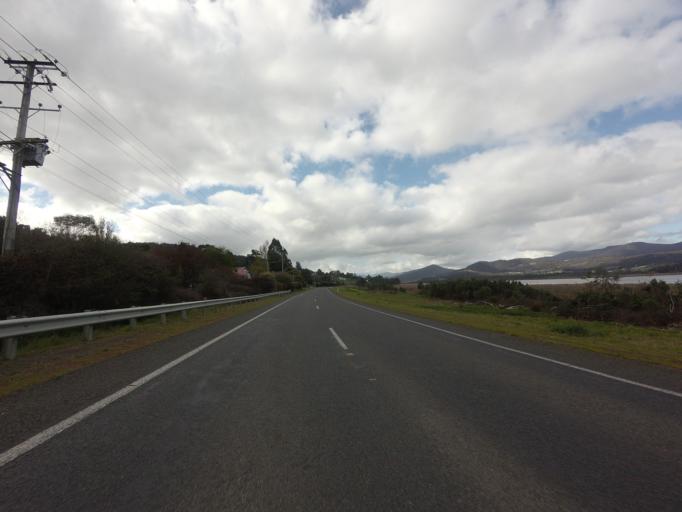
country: AU
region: Tasmania
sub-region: Huon Valley
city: Franklin
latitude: -43.1195
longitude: 146.9906
